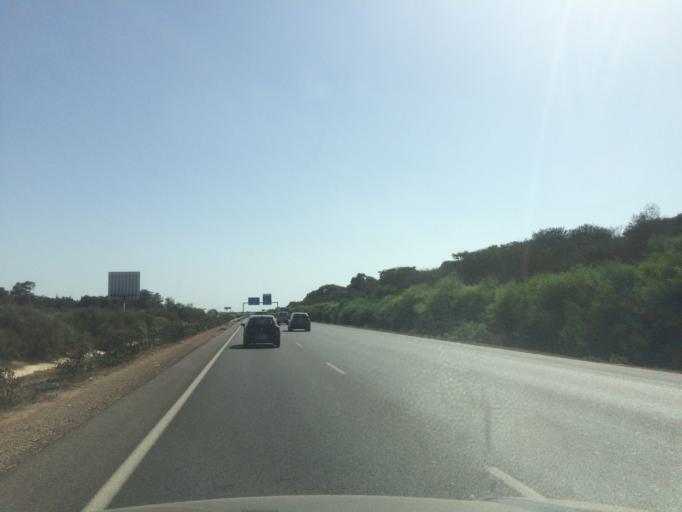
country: MA
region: Rabat-Sale-Zemmour-Zaer
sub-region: Skhirate-Temara
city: Temara
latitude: 33.9406
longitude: -6.9280
